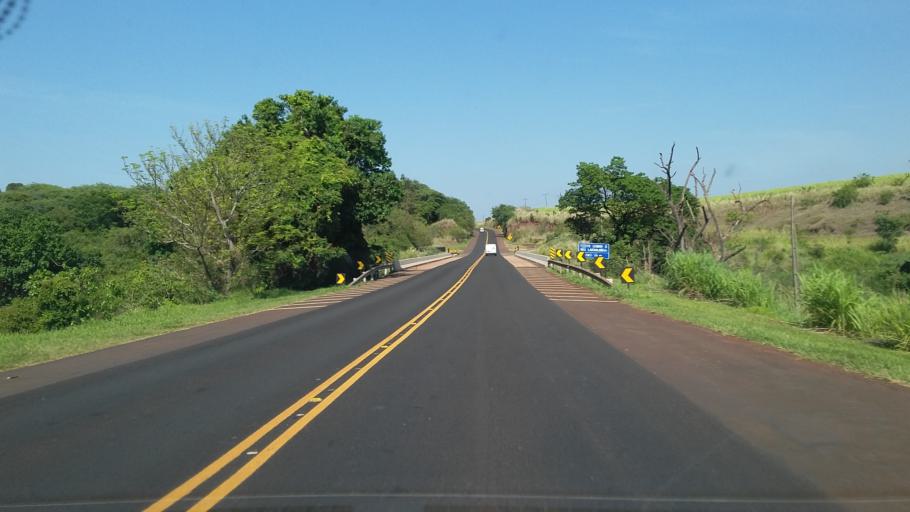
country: BR
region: Parana
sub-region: Bandeirantes
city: Bandeirantes
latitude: -23.1277
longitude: -50.4539
